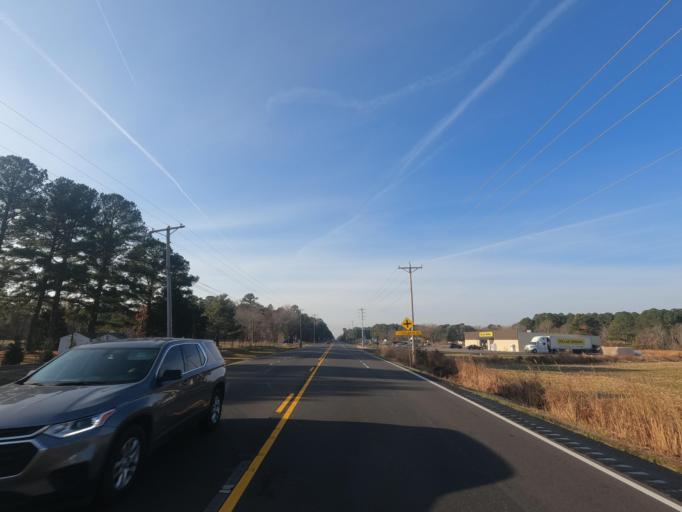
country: US
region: Maryland
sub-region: Somerset County
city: Crisfield
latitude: 38.0340
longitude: -75.7796
